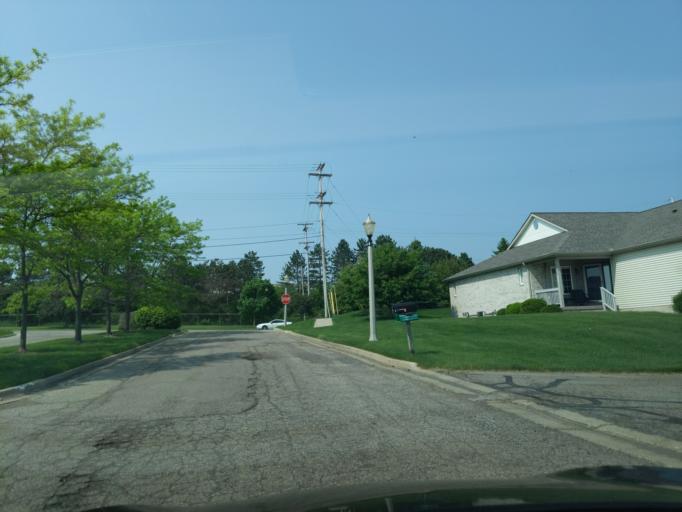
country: US
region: Michigan
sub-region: Eaton County
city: Waverly
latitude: 42.7549
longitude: -84.6554
